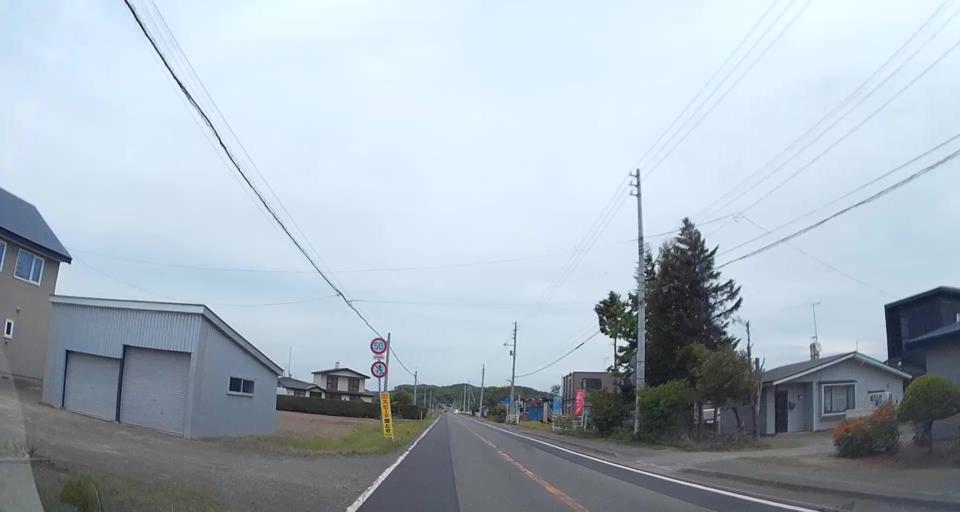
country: JP
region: Hokkaido
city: Chitose
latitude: 42.7294
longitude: 141.8839
